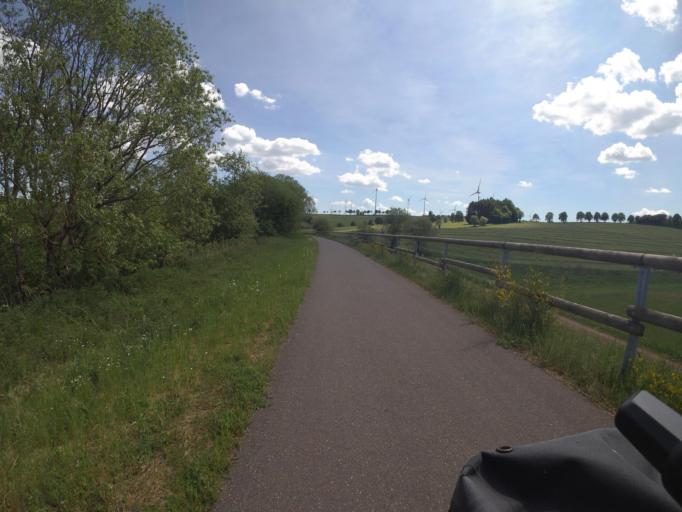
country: DE
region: Rheinland-Pfalz
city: Scheid
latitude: 50.3519
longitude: 6.4154
